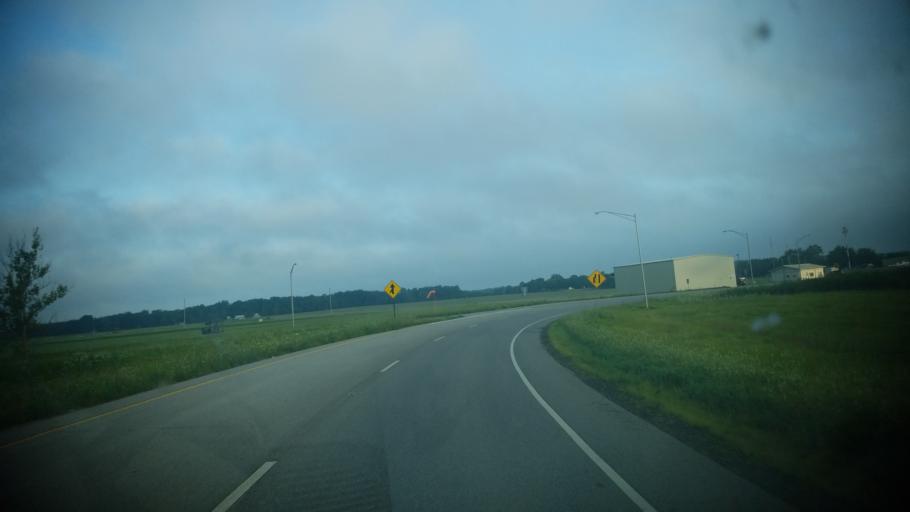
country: US
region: Illinois
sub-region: Wayne County
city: Fairfield
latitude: 38.3792
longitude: -88.4046
